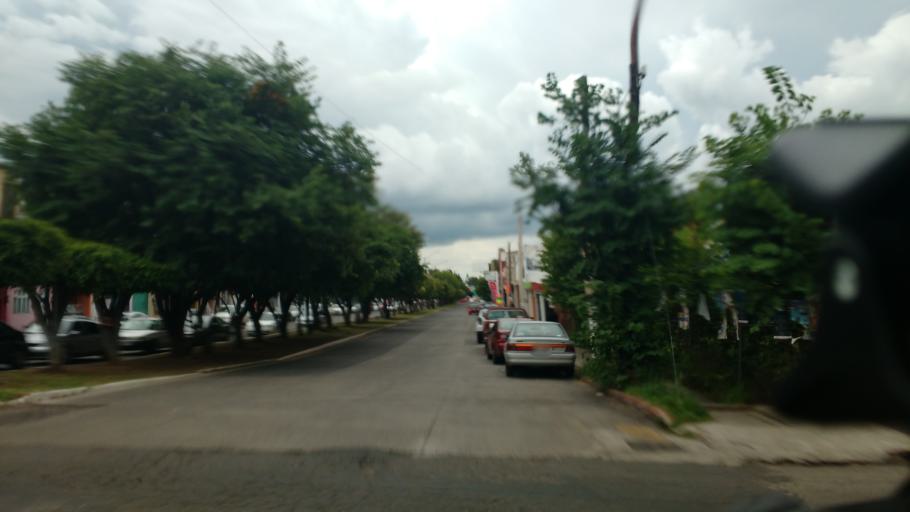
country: MX
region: Michoacan
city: Morelia
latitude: 19.6863
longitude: -101.1730
